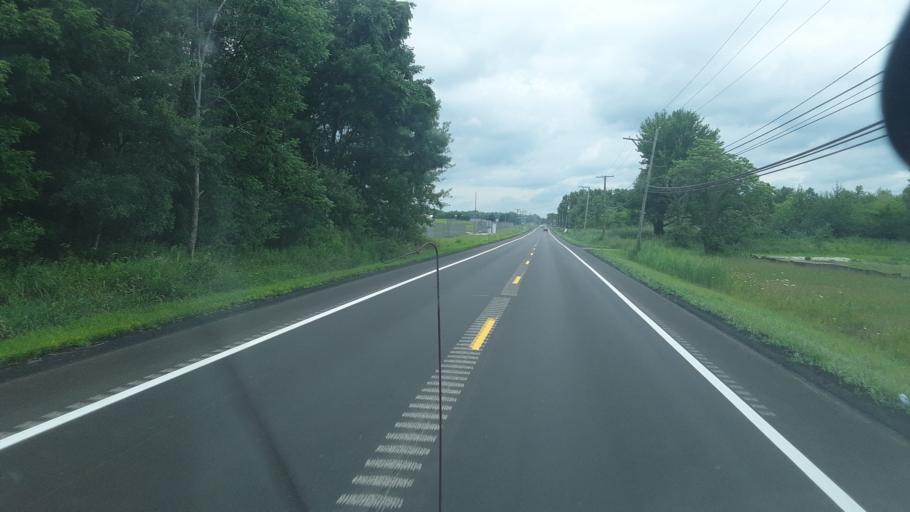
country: US
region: Ohio
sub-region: Trumbull County
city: Howland Center
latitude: 41.2496
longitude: -80.6638
